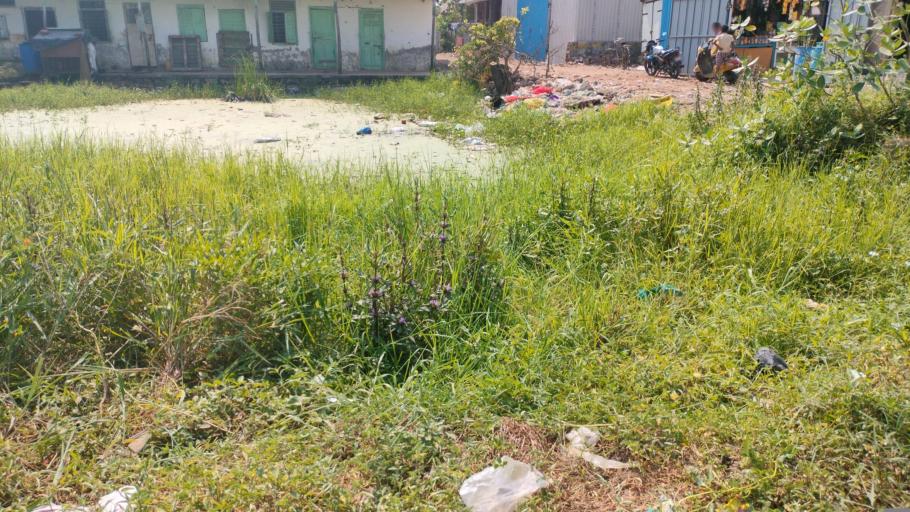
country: IN
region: Maharashtra
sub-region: Thane
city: Bhayandar
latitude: 19.2831
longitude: 72.7939
